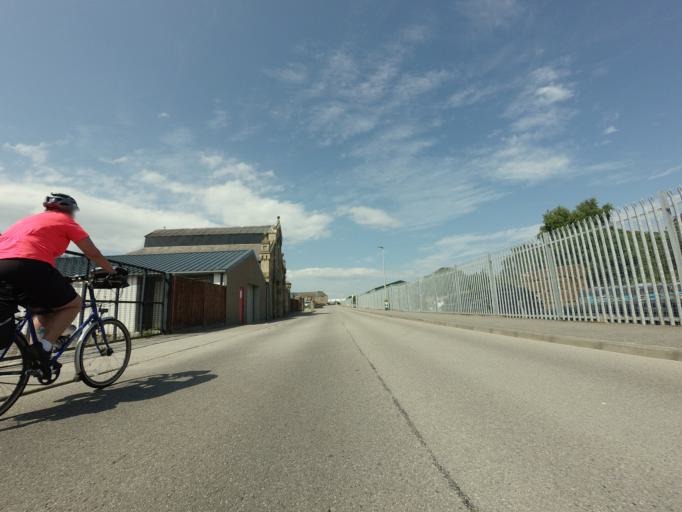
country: GB
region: Scotland
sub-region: Highland
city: Tain
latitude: 57.8146
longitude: -4.0545
